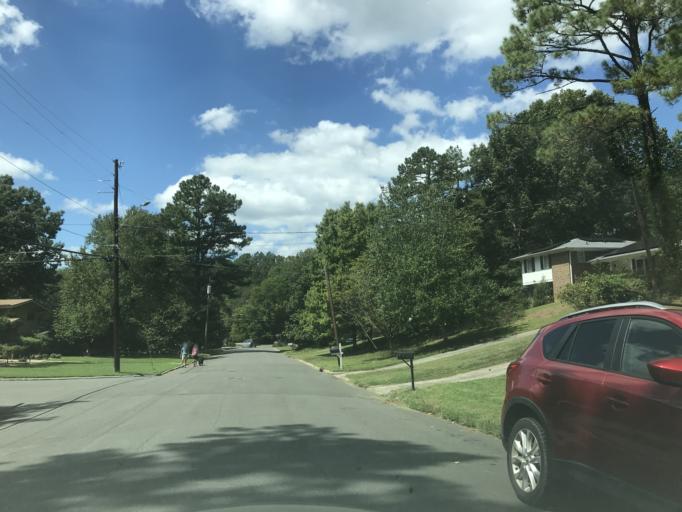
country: US
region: North Carolina
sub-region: Orange County
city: Chapel Hill
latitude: 35.9268
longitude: -79.0176
